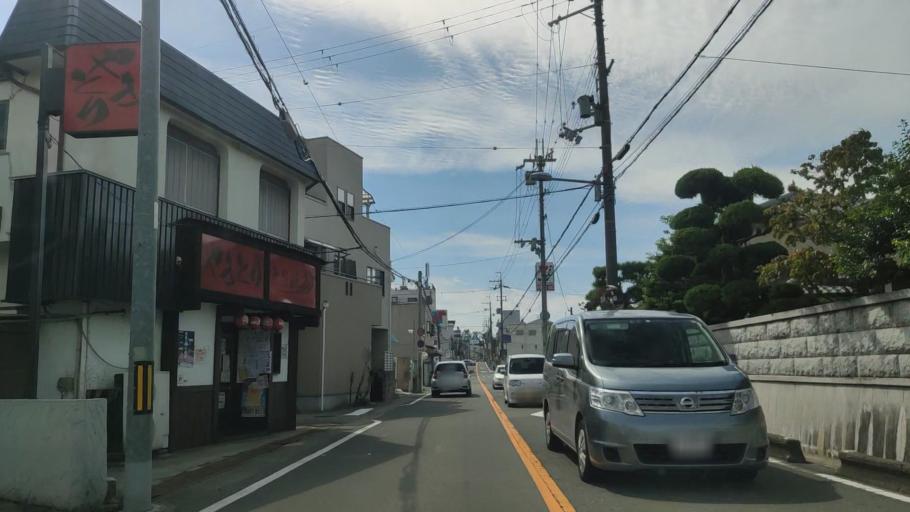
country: JP
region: Osaka
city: Toyonaka
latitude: 34.7953
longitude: 135.4644
